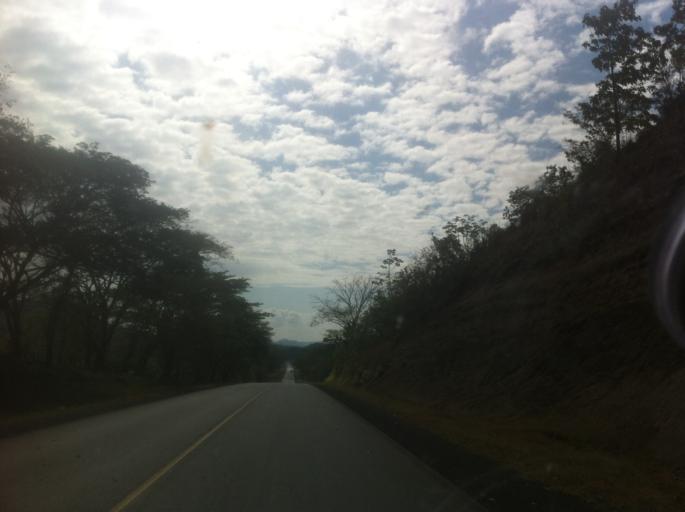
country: NI
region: Rio San Juan
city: San Miguelito
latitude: 11.3778
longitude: -84.7839
